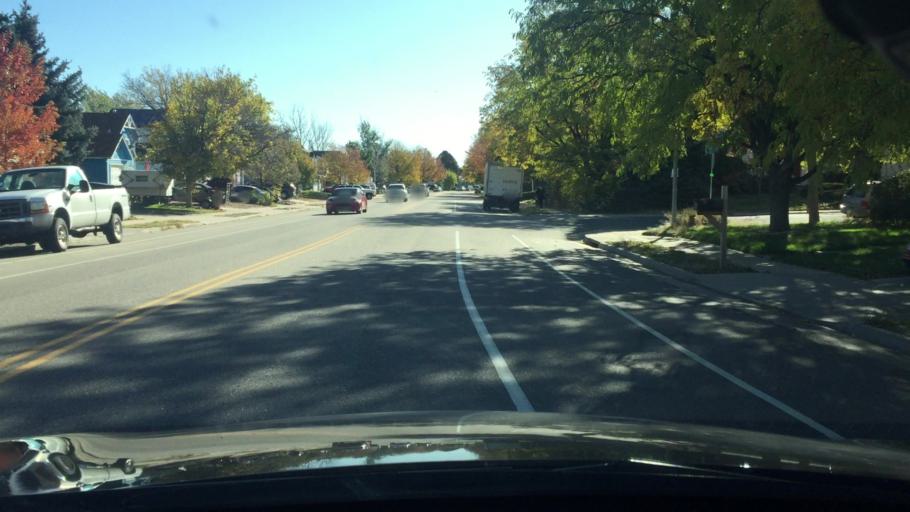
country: US
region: Colorado
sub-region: Arapahoe County
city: Dove Valley
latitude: 39.6306
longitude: -104.7895
